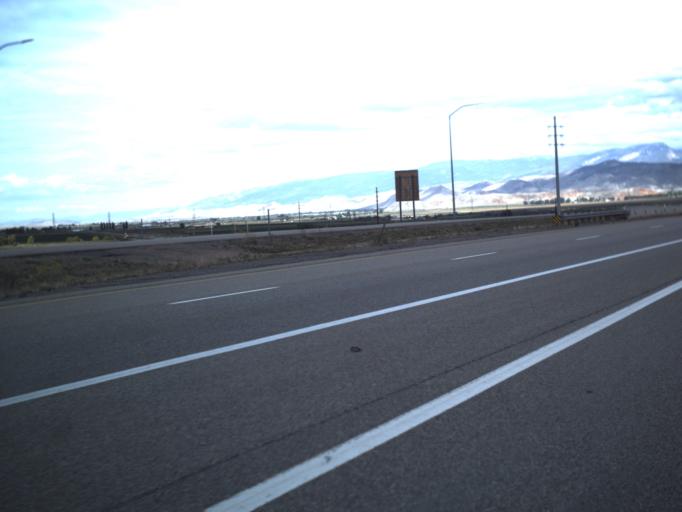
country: US
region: Utah
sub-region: Sevier County
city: Aurora
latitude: 38.8754
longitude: -111.9606
